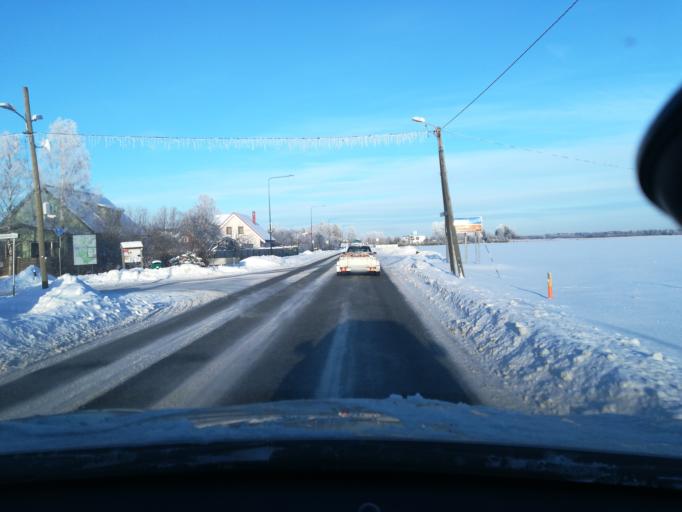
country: EE
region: Harju
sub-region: Saue linn
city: Saue
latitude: 59.3308
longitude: 24.5483
